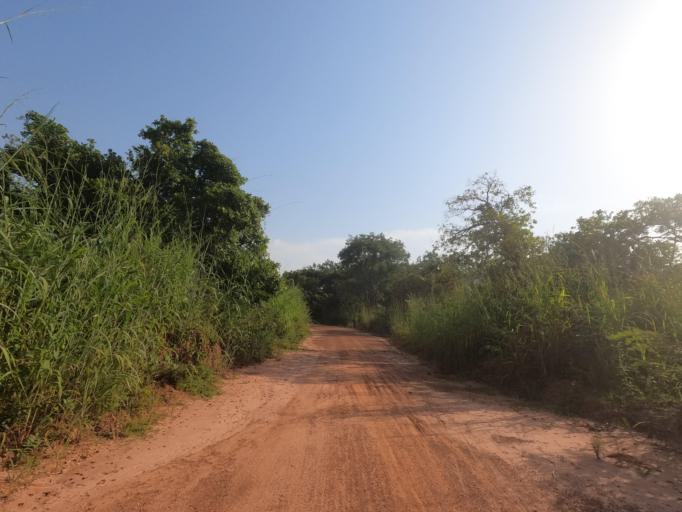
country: SN
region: Sedhiou
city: Sedhiou
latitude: 12.4182
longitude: -15.7327
